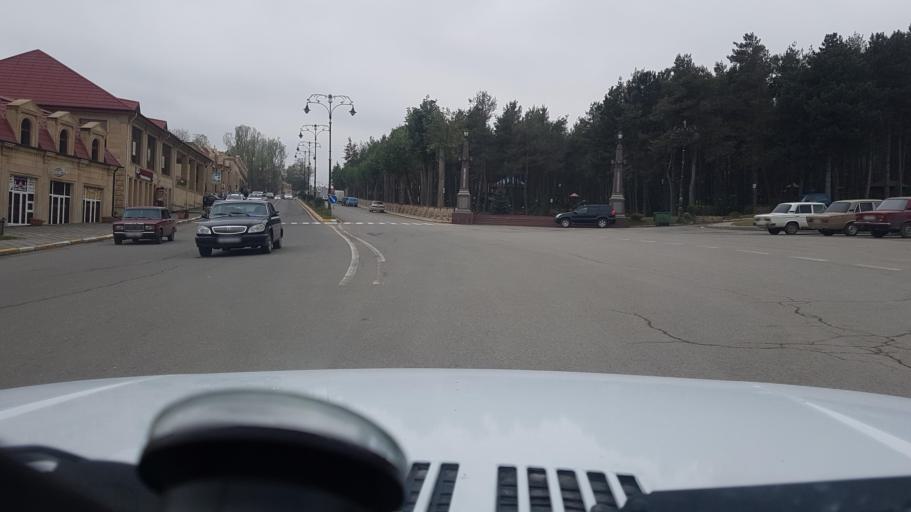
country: AZ
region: Gadabay Rayon
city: Kyadabek
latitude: 40.5797
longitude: 45.8088
